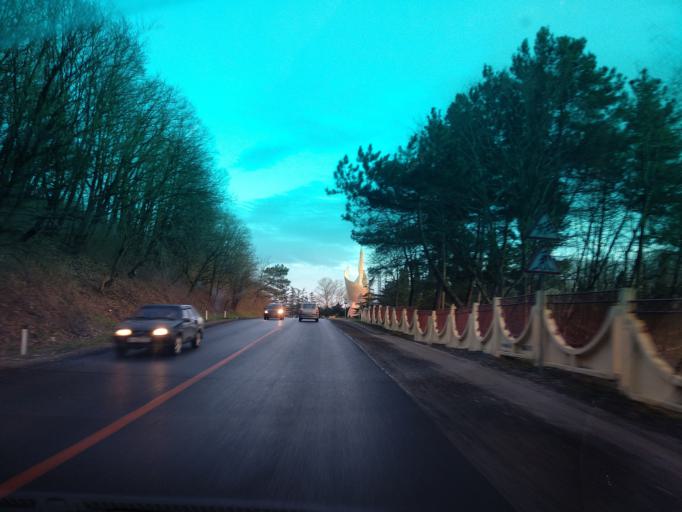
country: RU
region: Krasnodarskiy
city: Novomikhaylovskiy
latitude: 44.2566
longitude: 38.8294
